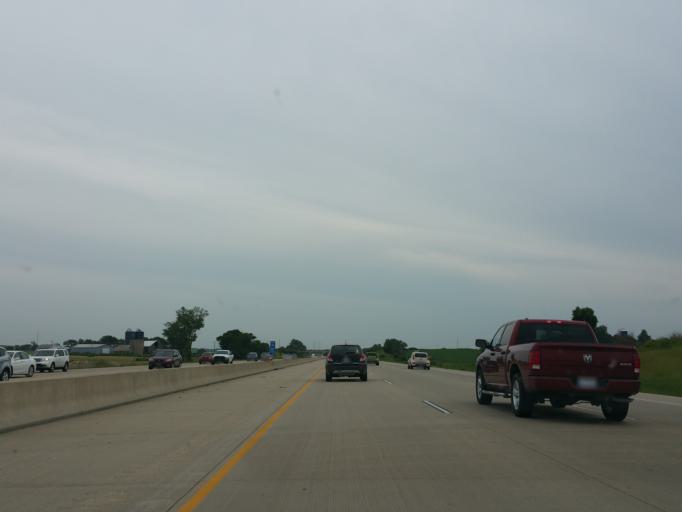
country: US
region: Wisconsin
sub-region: Columbia County
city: Poynette
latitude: 43.3016
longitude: -89.4257
